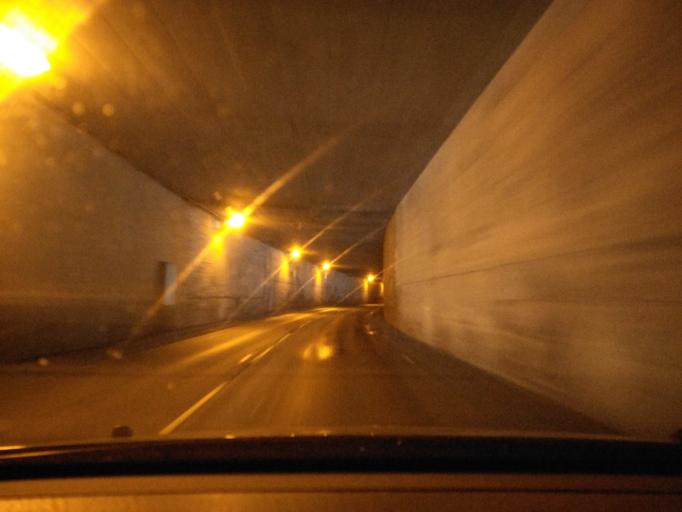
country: NO
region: Hordaland
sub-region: Odda
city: Odda
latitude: 59.8491
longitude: 6.9606
